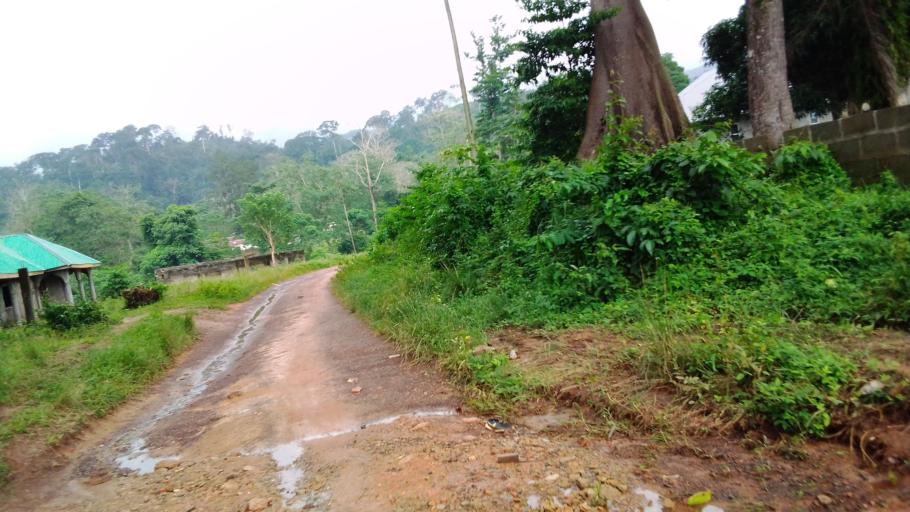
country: SL
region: Eastern Province
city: Kenema
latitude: 7.8885
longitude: -11.1945
